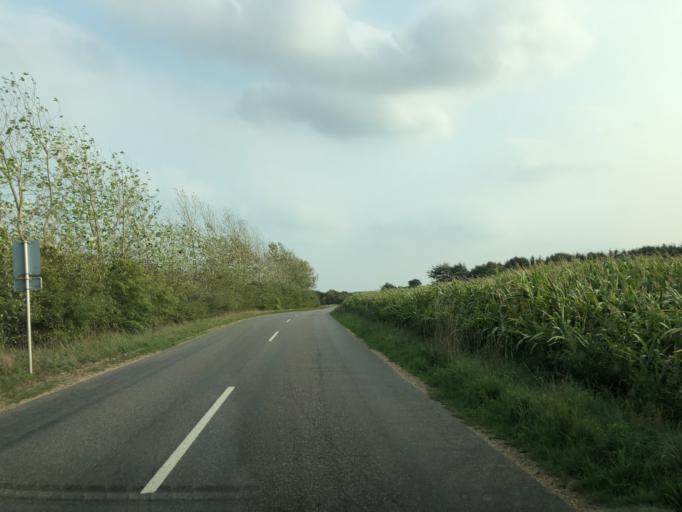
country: DK
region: Central Jutland
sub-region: Ringkobing-Skjern Kommune
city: Videbaek
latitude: 56.0826
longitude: 8.7041
